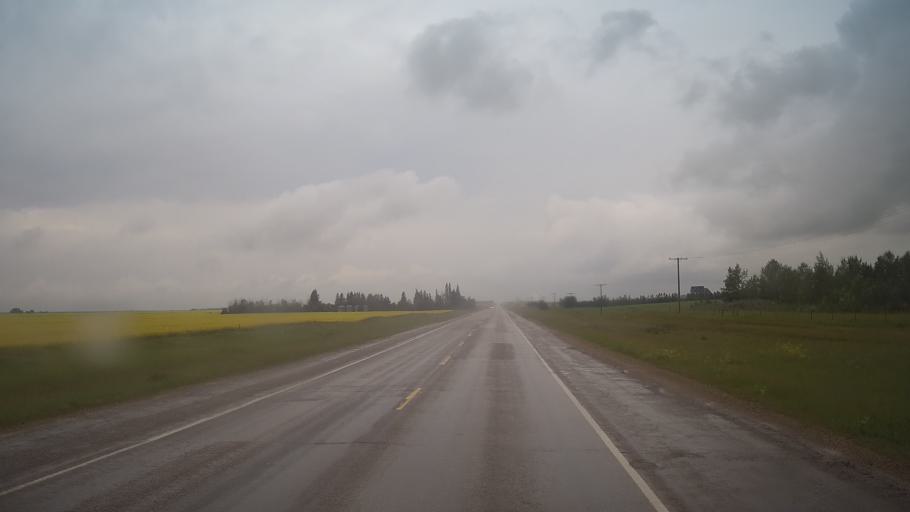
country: CA
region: Saskatchewan
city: Unity
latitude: 52.4350
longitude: -109.0302
